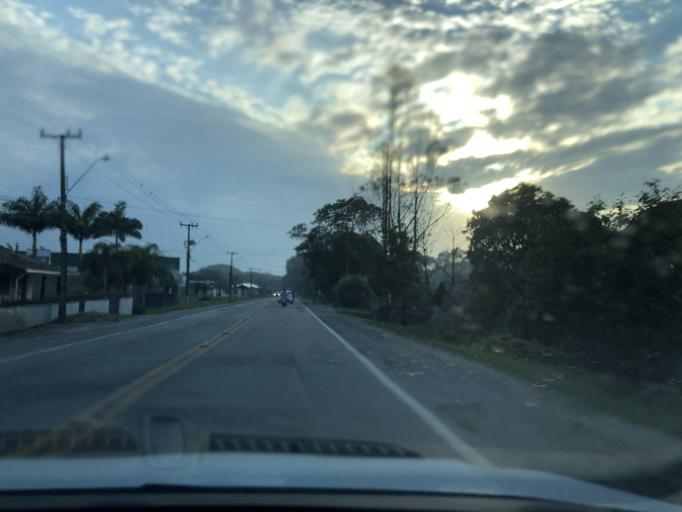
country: BR
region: Santa Catarina
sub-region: Sao Francisco Do Sul
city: Sao Francisco do Sul
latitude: -26.2468
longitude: -48.6044
